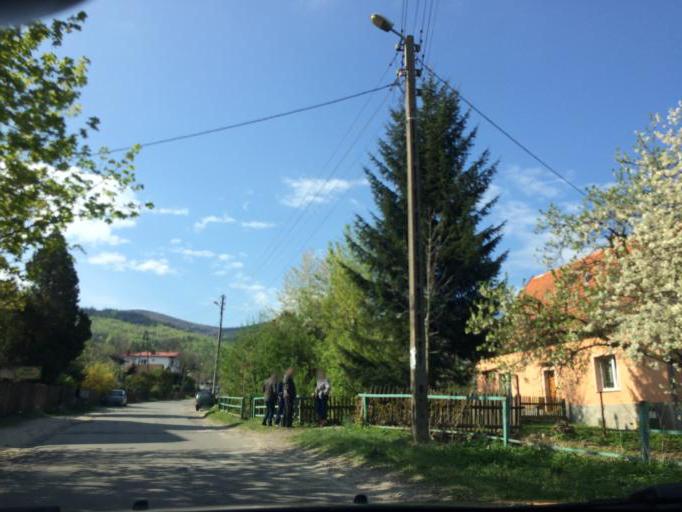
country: PL
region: Lower Silesian Voivodeship
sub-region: Powiat dzierzoniowski
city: Pieszyce
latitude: 50.6753
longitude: 16.5443
